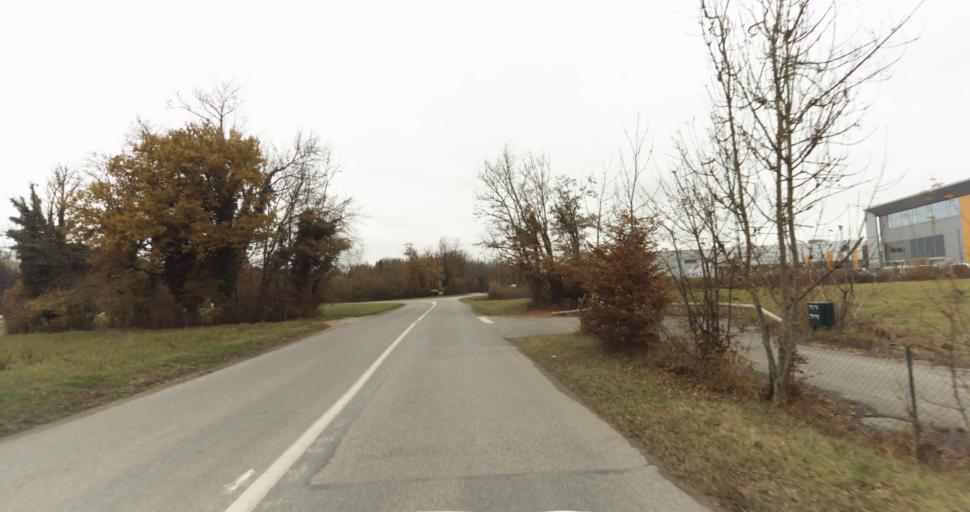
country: FR
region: Rhone-Alpes
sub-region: Departement de la Haute-Savoie
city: Viuz-la-Chiesaz
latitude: 45.8442
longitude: 6.0555
